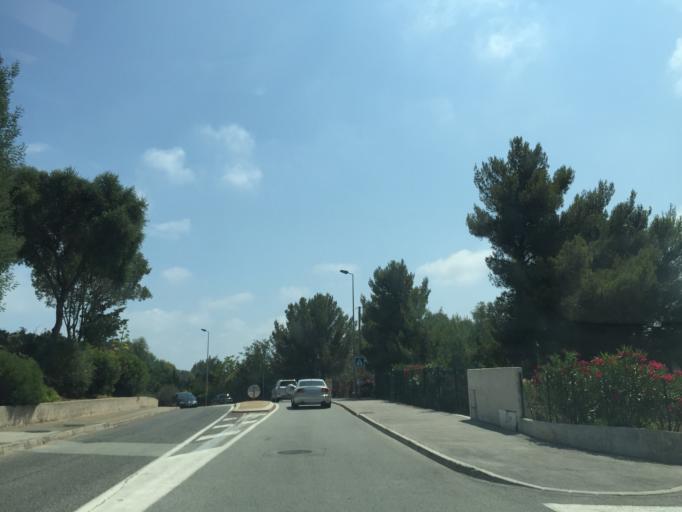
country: FR
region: Provence-Alpes-Cote d'Azur
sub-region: Departement du Var
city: Saint-Raphael
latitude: 43.4323
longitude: 6.8692
